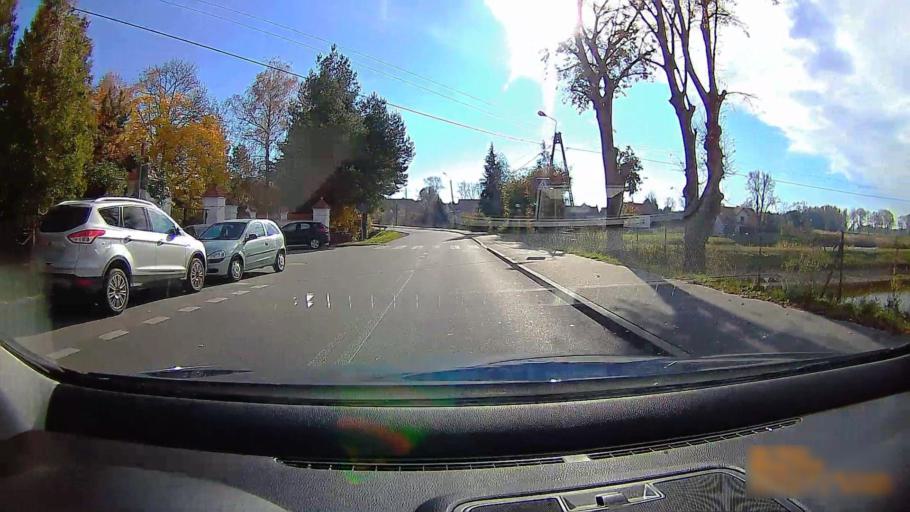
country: PL
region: Greater Poland Voivodeship
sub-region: Powiat ostrzeszowski
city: Doruchow
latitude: 51.3617
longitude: 18.0285
